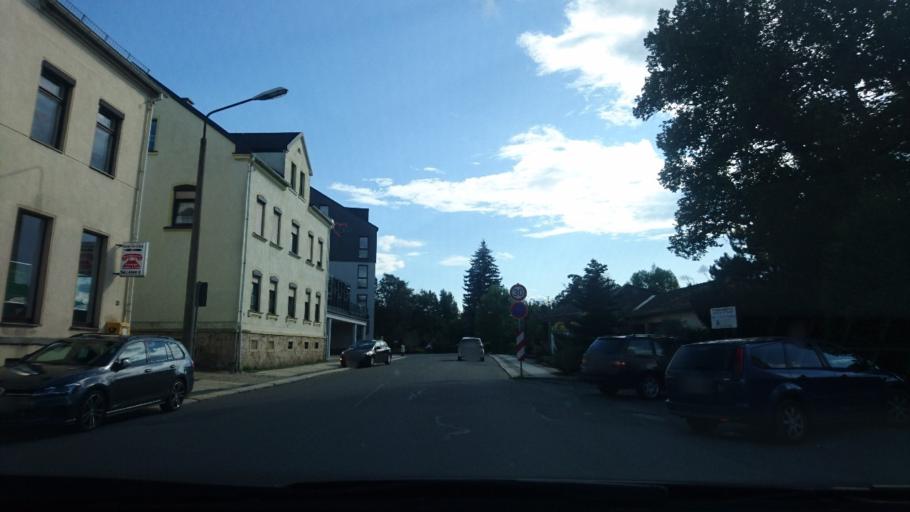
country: DE
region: Saxony
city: Rodewisch
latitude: 50.5269
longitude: 12.4042
